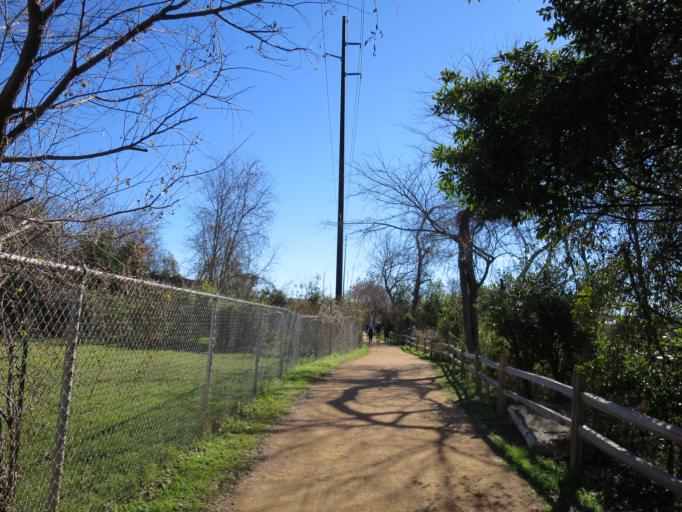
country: US
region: Texas
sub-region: Travis County
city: Rollingwood
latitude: 30.2761
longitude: -97.7731
